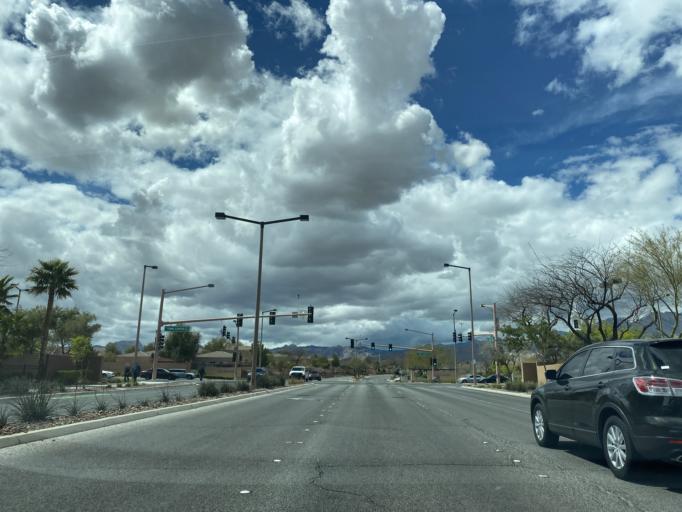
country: US
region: Nevada
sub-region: Clark County
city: Summerlin South
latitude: 36.1676
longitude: -115.3237
